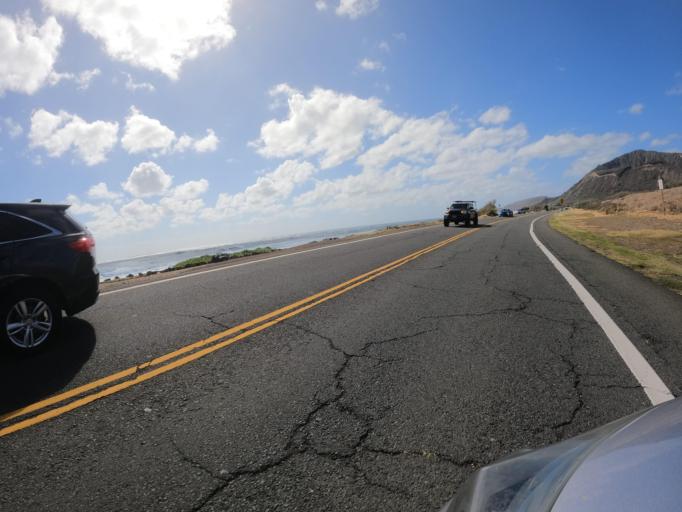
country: US
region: Hawaii
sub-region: Honolulu County
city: Waimanalo Beach
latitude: 21.2940
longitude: -157.6595
